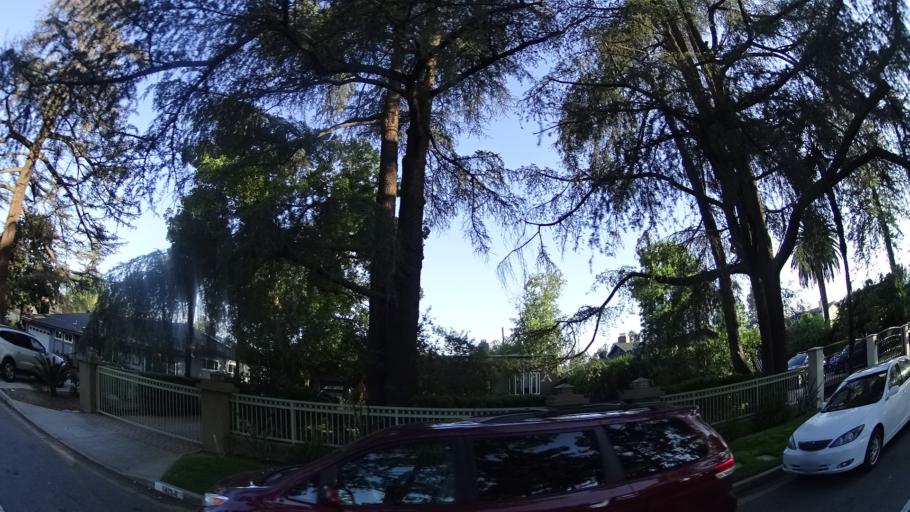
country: US
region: California
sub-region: Los Angeles County
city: Sherman Oaks
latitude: 34.1684
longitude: -118.4413
